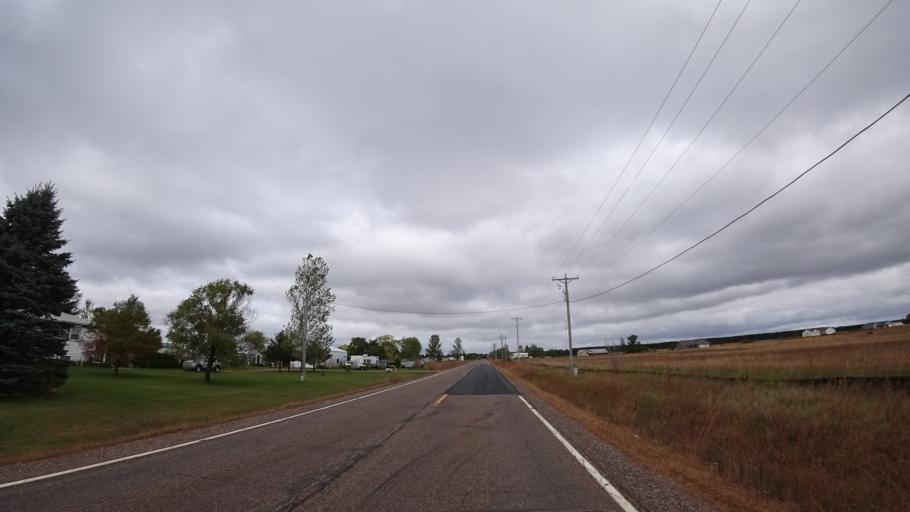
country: US
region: Wisconsin
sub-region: Chippewa County
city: Lake Wissota
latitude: 44.9339
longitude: -91.2678
